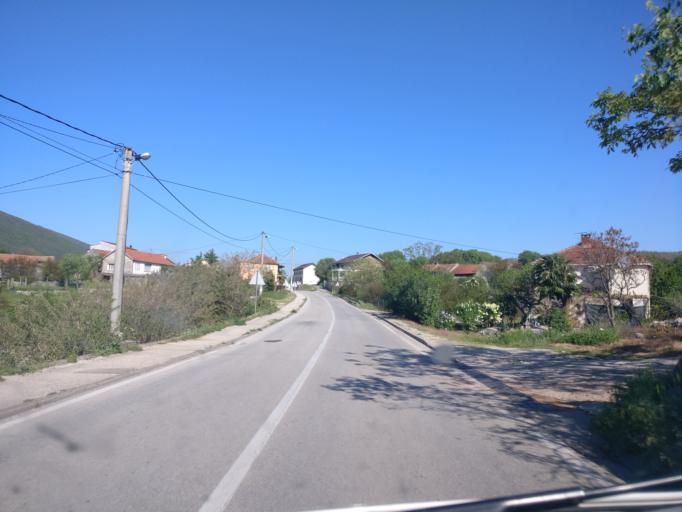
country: BA
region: Federation of Bosnia and Herzegovina
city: Capljina
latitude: 43.1265
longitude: 17.6807
